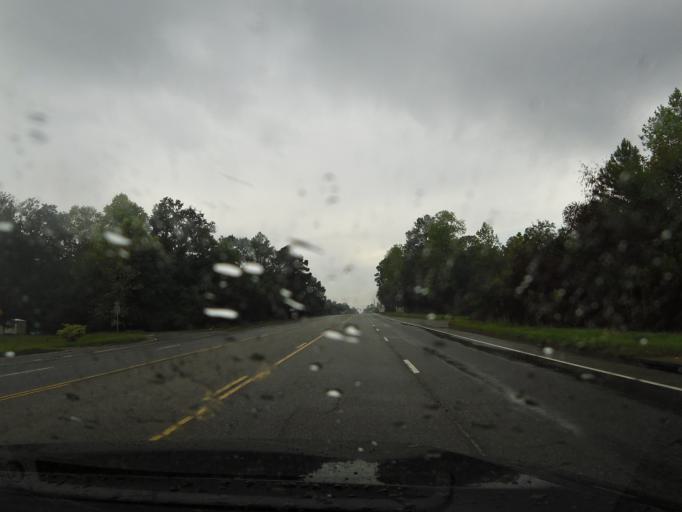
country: US
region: Georgia
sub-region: Wayne County
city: Jesup
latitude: 31.5909
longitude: -81.8656
